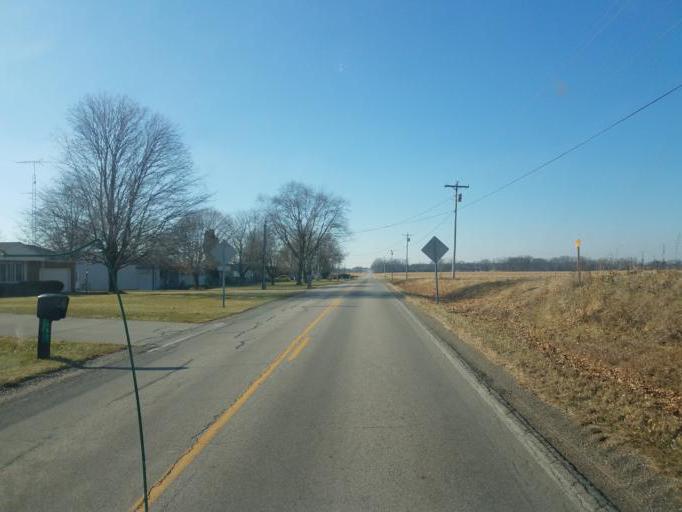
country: US
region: Ohio
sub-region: Marion County
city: Marion
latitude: 40.6446
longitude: -83.1475
